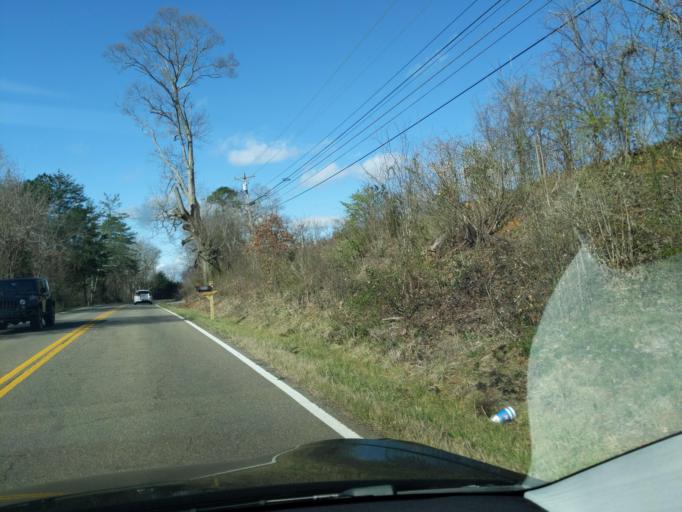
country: US
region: Tennessee
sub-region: Jefferson County
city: Dandridge
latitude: 35.9705
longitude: -83.5079
